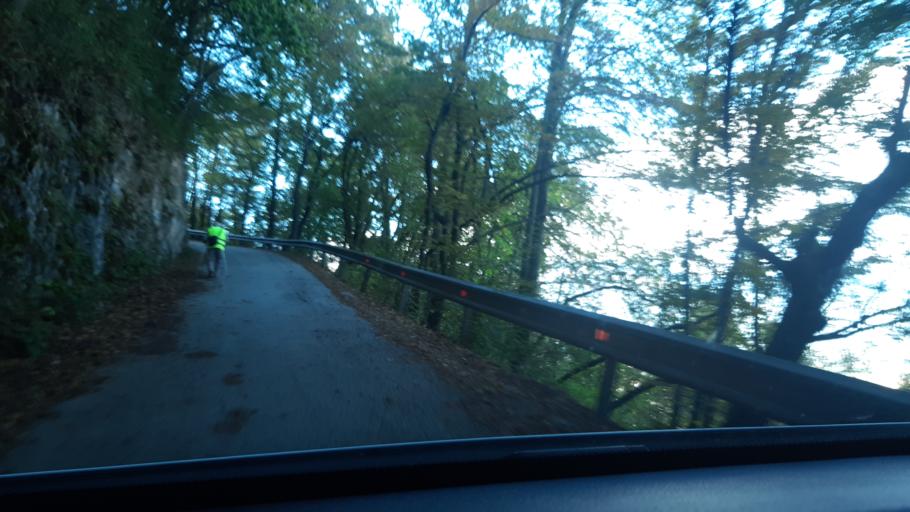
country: SI
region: Kranj
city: Kranj
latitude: 46.2417
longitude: 14.3441
